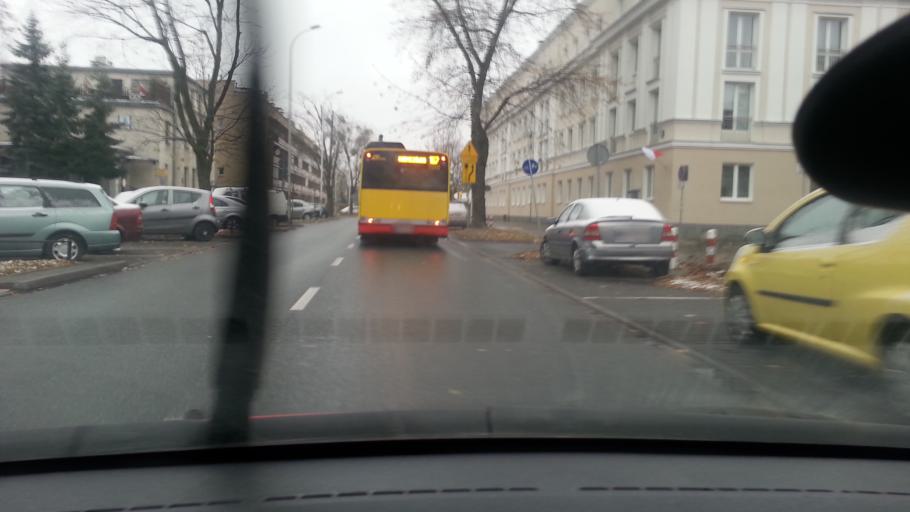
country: PL
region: Masovian Voivodeship
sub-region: Warszawa
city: Bemowo
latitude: 52.2442
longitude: 20.9479
